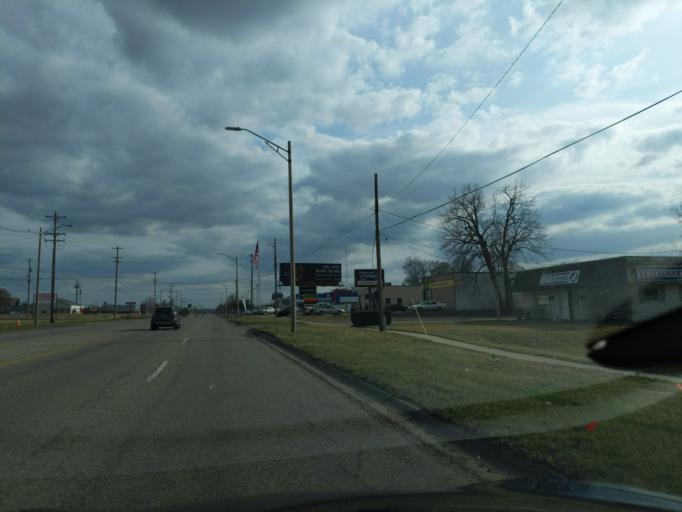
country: US
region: Michigan
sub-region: Ingham County
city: Holt
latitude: 42.6786
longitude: -84.5383
